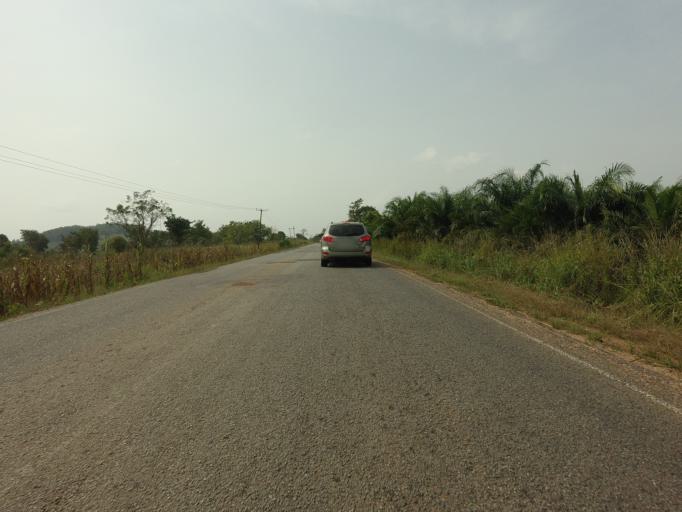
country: GH
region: Volta
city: Ho
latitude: 6.3537
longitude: 0.1761
